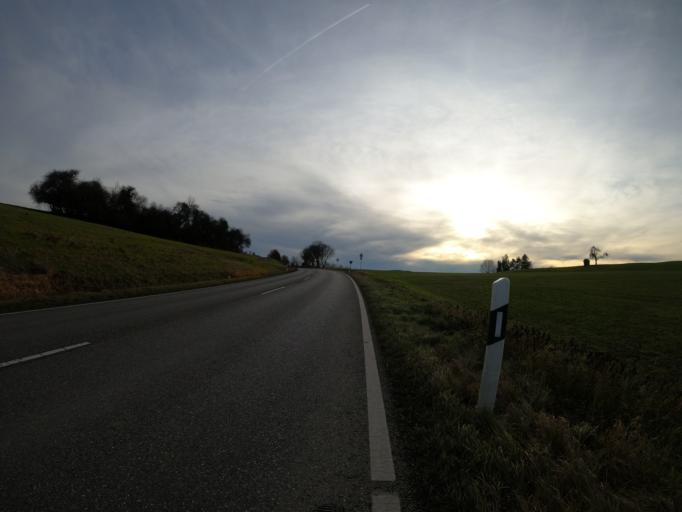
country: DE
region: Baden-Wuerttemberg
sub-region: Regierungsbezirk Stuttgart
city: Goeppingen
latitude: 48.6823
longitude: 9.6634
